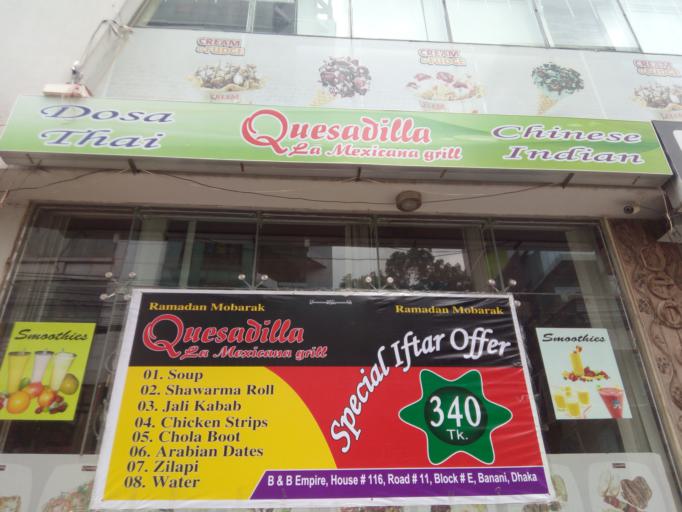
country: BD
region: Dhaka
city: Paltan
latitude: 23.7903
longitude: 90.4083
